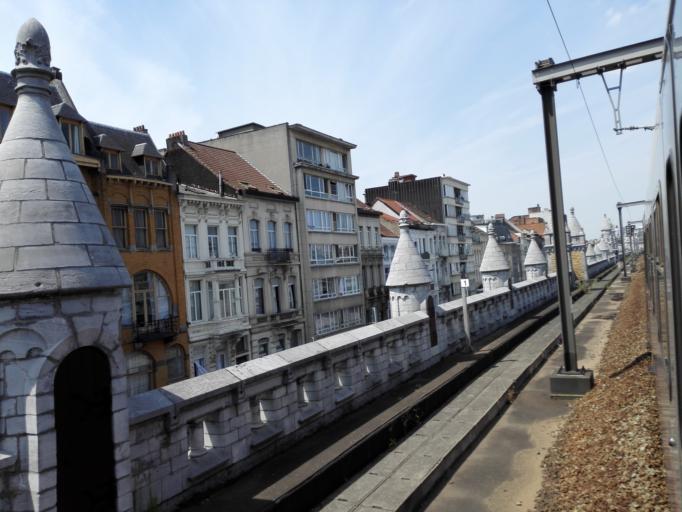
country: BE
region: Flanders
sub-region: Provincie Antwerpen
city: Antwerpen
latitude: 51.2069
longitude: 4.4253
